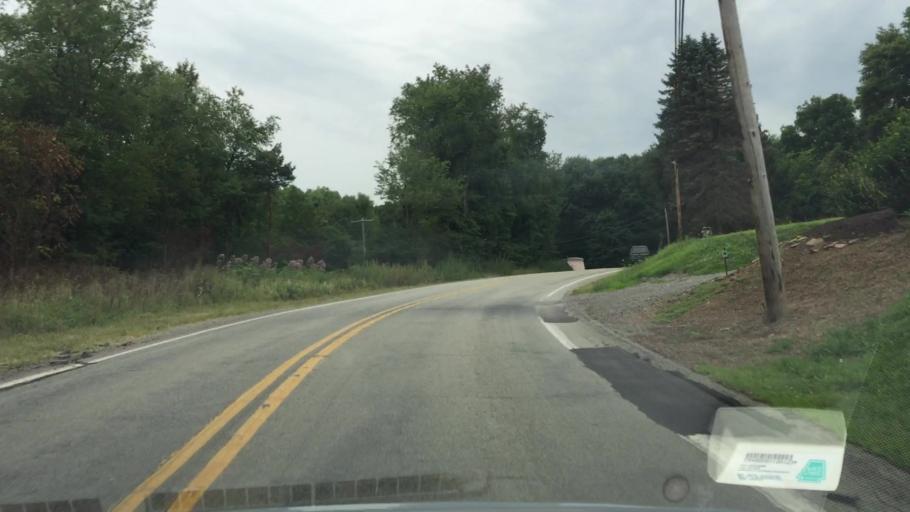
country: US
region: Pennsylvania
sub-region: Allegheny County
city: Curtisville
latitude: 40.6685
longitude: -79.8314
